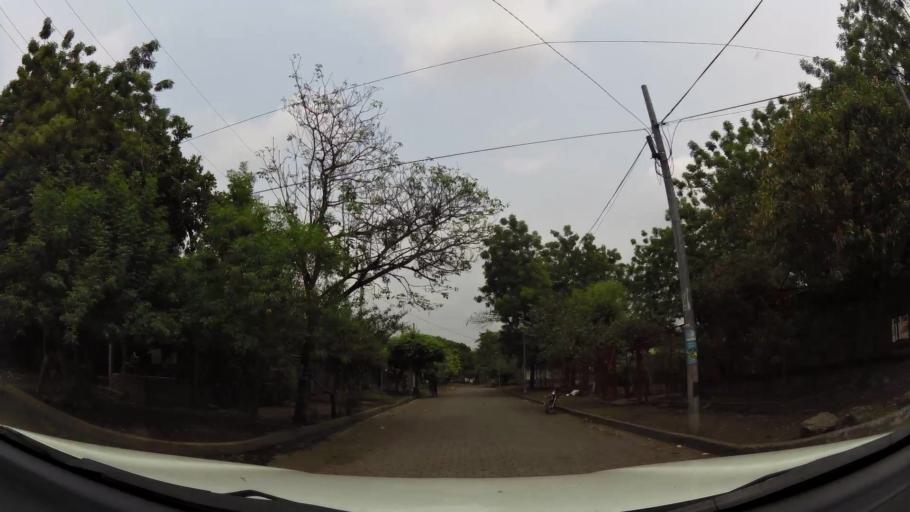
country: NI
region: Chinandega
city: Chinandega
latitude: 12.6507
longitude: -87.1234
